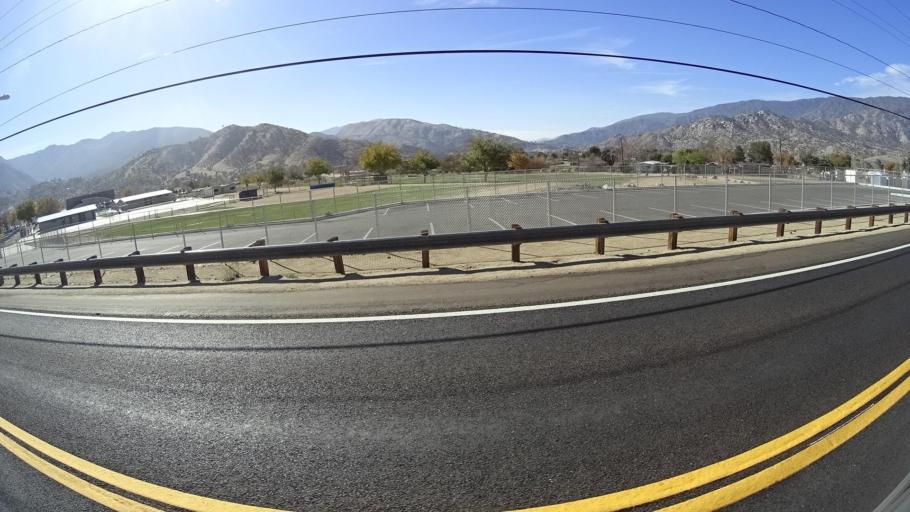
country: US
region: California
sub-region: Kern County
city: Lake Isabella
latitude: 35.6117
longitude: -118.4663
